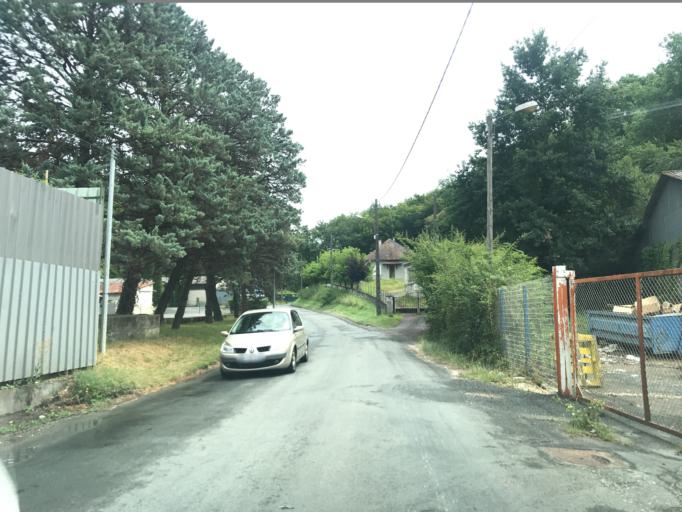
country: FR
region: Aquitaine
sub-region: Departement de la Dordogne
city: Chancelade
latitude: 45.1814
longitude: 0.6677
